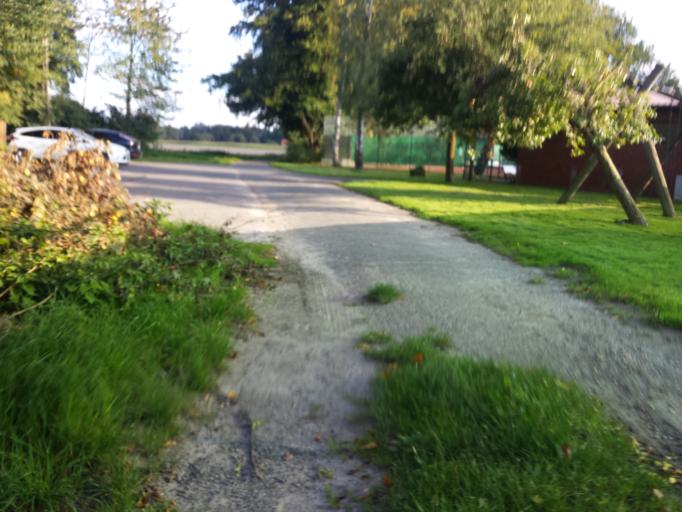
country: DE
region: North Rhine-Westphalia
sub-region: Regierungsbezirk Detmold
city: Langenberg
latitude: 51.7582
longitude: 8.3320
